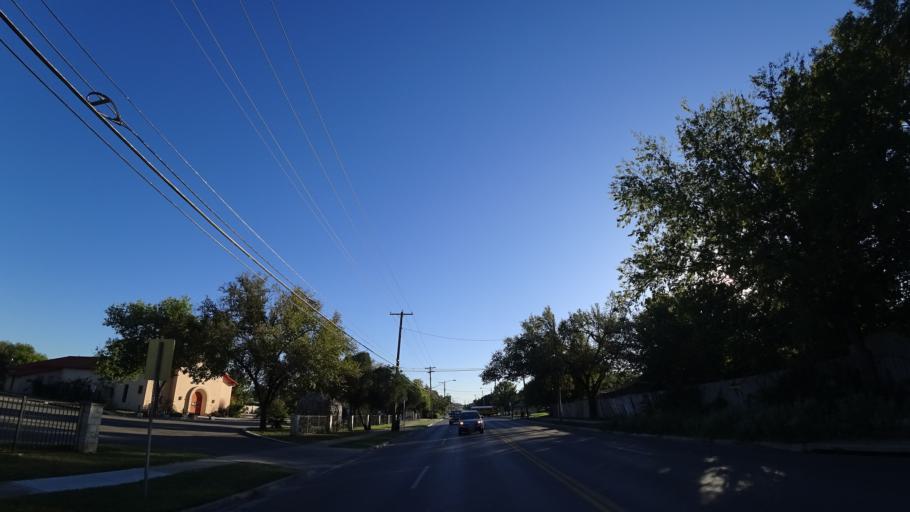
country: US
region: Texas
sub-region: Travis County
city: Austin
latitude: 30.2328
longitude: -97.6984
